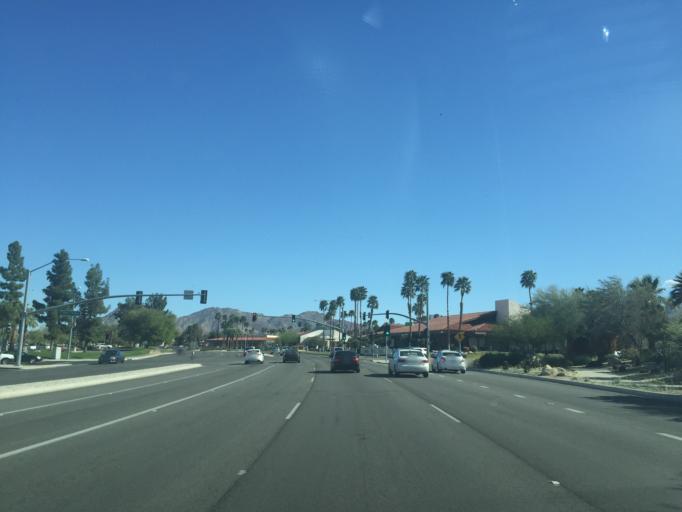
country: US
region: California
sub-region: Riverside County
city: Rancho Mirage
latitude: 33.7236
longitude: -116.3993
